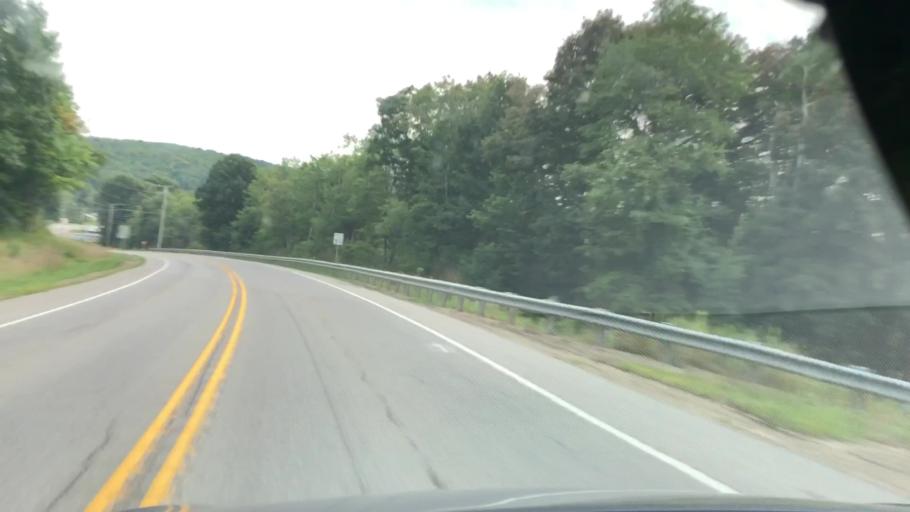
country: US
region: Pennsylvania
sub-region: Crawford County
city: Titusville
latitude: 41.5410
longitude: -79.7145
